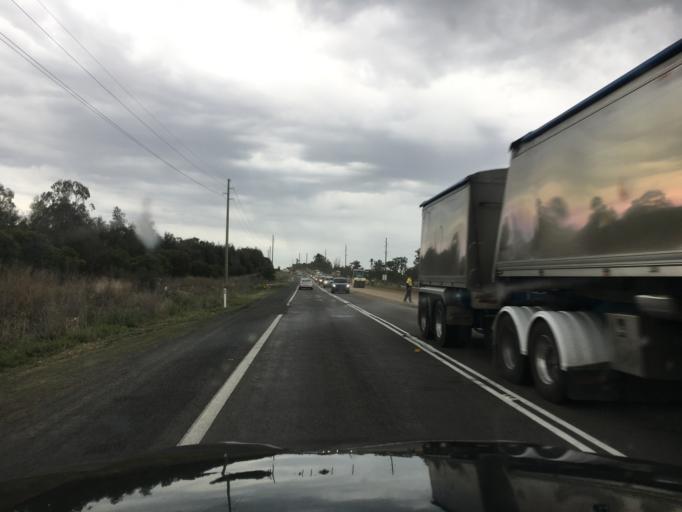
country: AU
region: New South Wales
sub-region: Muswellbrook
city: Muswellbrook
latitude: -32.1986
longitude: 150.8930
